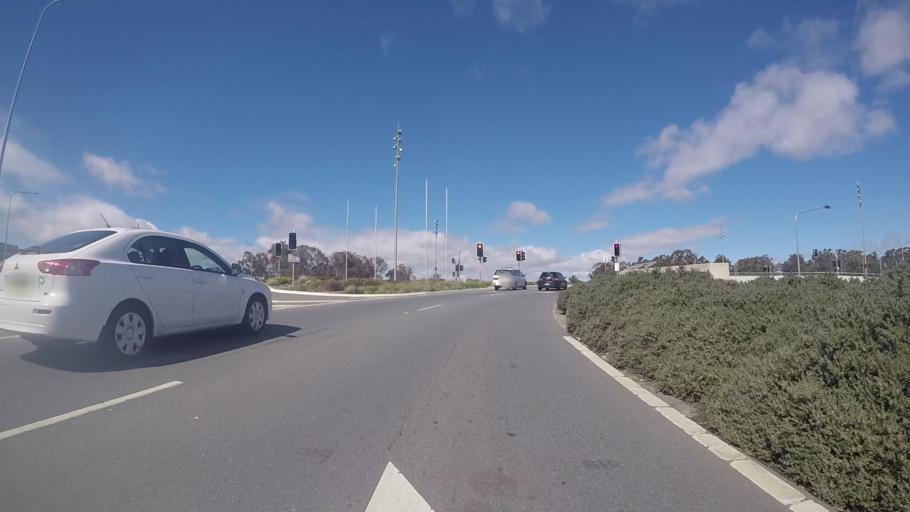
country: AU
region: Australian Capital Territory
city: Canberra
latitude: -35.2984
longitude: 149.1480
